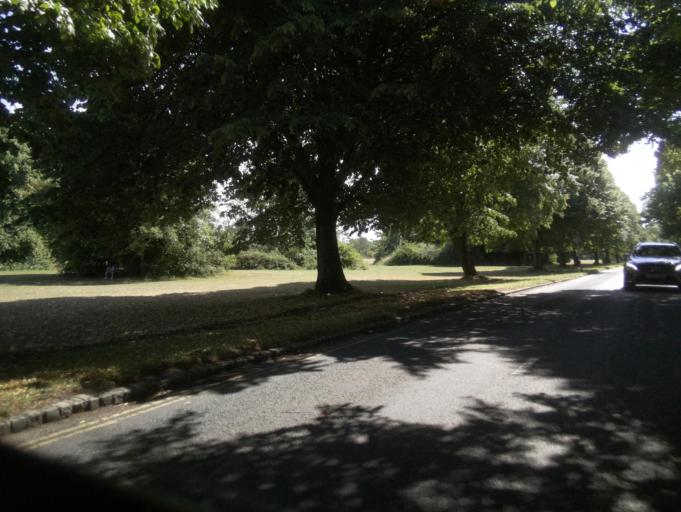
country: GB
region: England
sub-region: Bristol
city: Bristol
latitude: 51.4668
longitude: -2.6253
